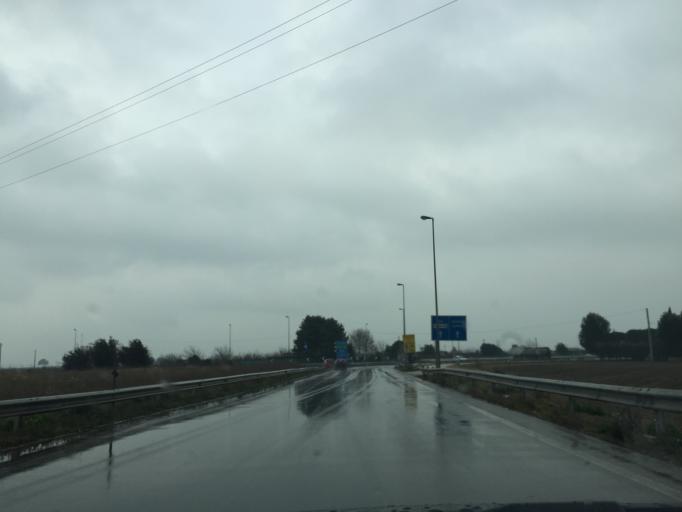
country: IT
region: Apulia
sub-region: Provincia di Foggia
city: Foggia
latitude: 41.4724
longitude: 15.5078
